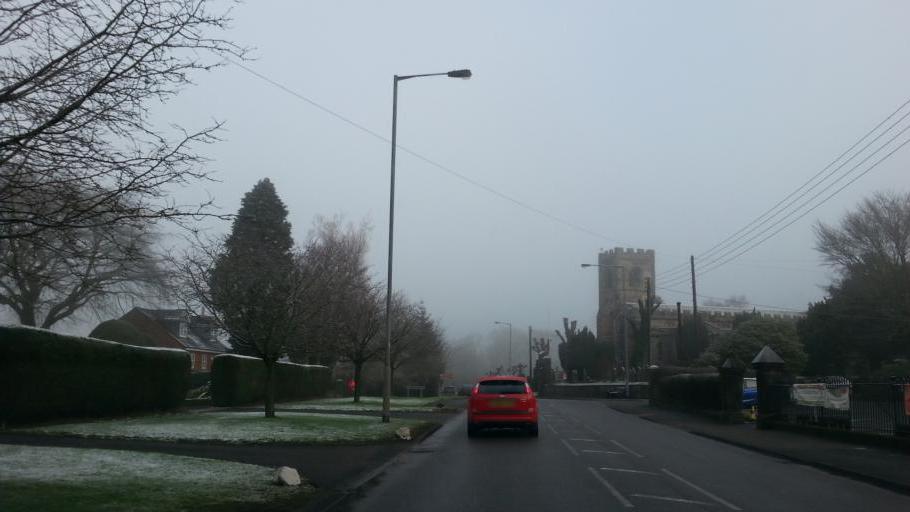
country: GB
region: England
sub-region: Staffordshire
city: Biddulph
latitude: 53.1275
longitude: -2.1667
